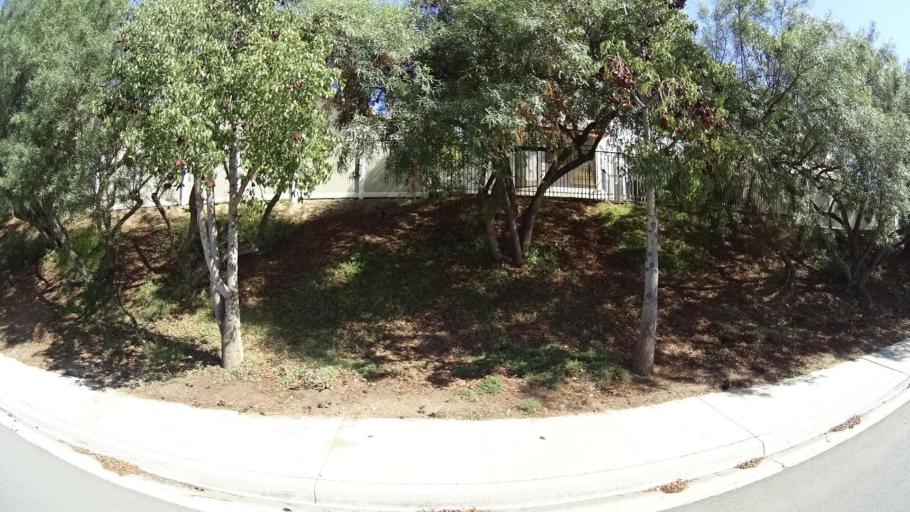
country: US
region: California
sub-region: San Diego County
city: Rancho San Diego
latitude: 32.7568
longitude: -116.9350
